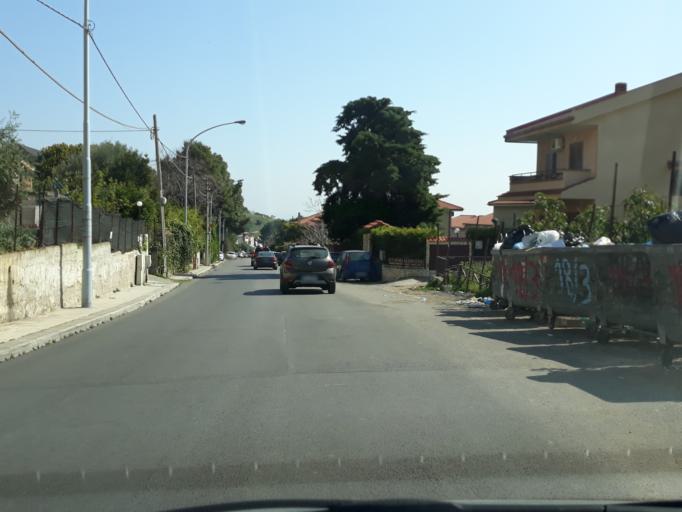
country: IT
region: Sicily
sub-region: Palermo
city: Piano dei Geli
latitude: 38.1175
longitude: 13.2949
